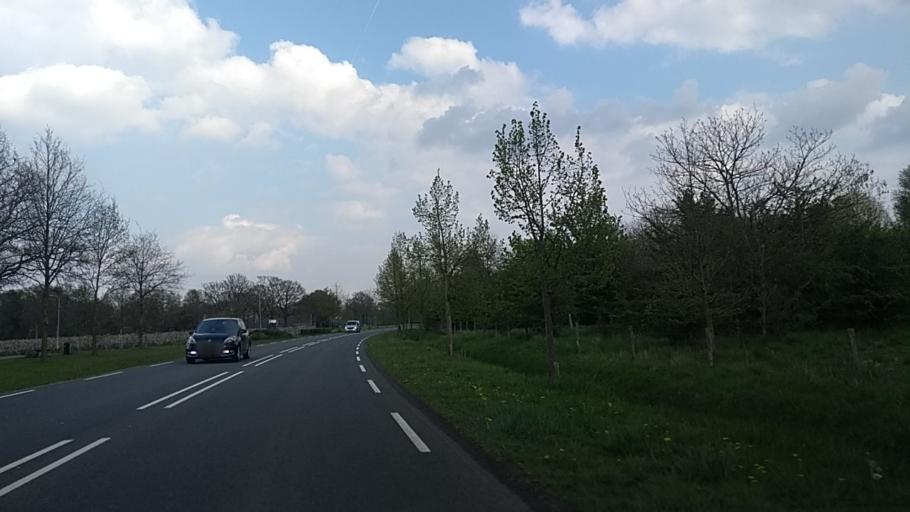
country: NL
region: Limburg
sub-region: Gemeente Peel en Maas
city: Maasbree
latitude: 51.4168
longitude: 6.0391
